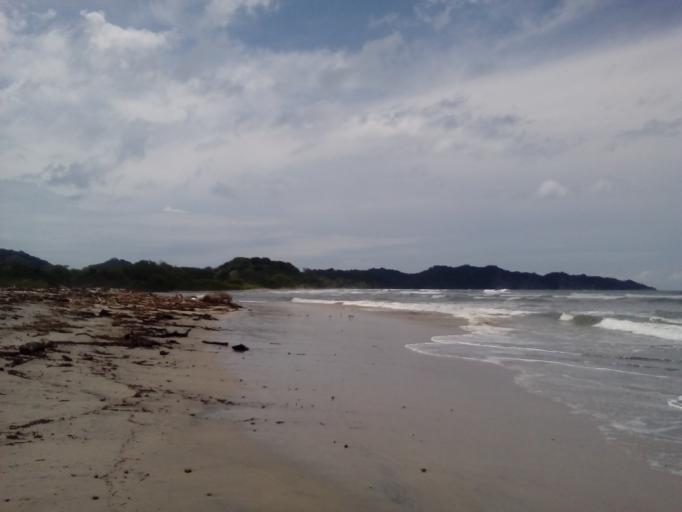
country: CR
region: Guanacaste
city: Samara
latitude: 9.9300
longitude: -85.6625
